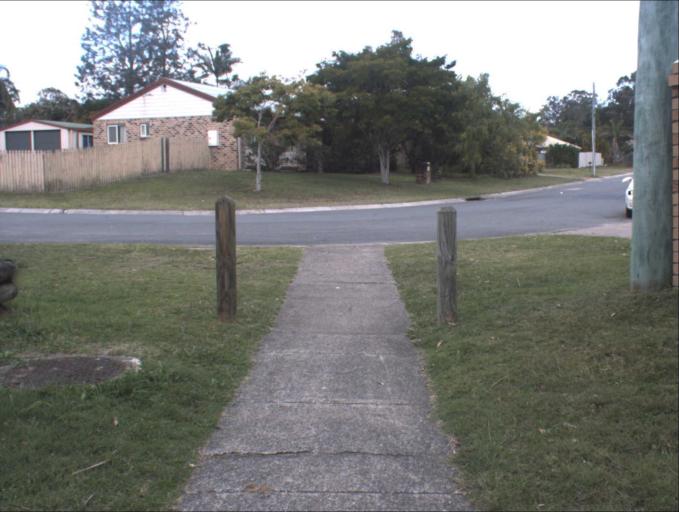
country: AU
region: Queensland
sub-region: Logan
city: Waterford West
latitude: -27.6772
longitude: 153.0988
